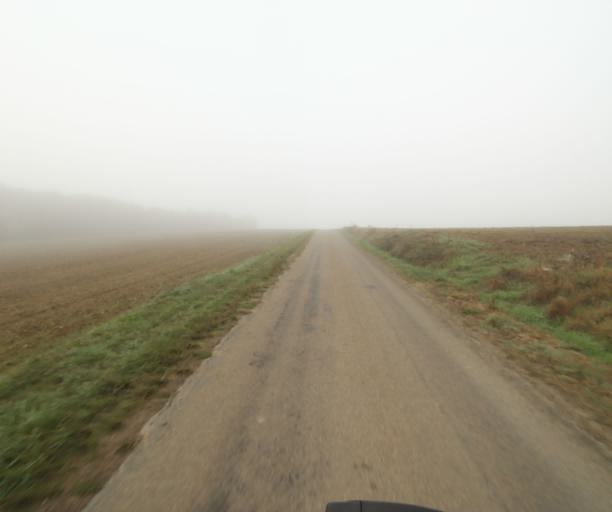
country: FR
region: Midi-Pyrenees
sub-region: Departement du Tarn-et-Garonne
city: Nohic
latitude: 43.9333
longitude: 1.4753
